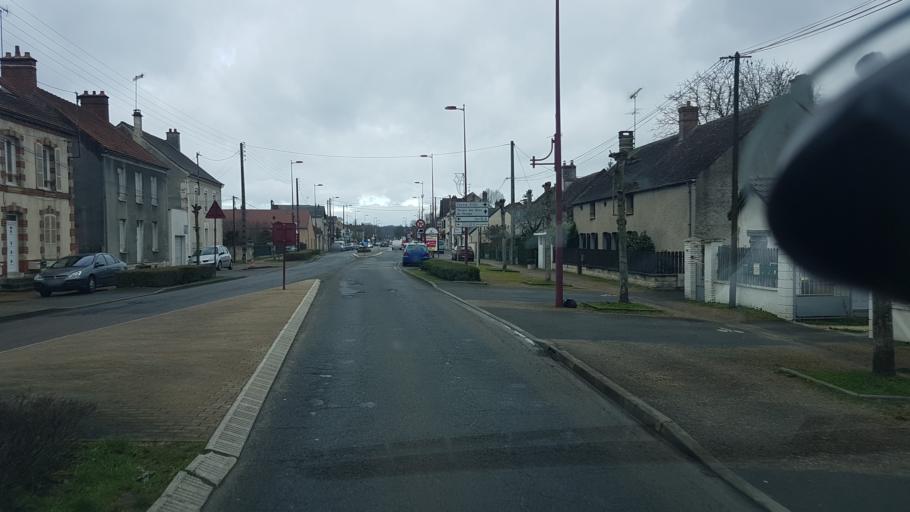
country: FR
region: Centre
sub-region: Departement du Loiret
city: Dordives
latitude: 48.1457
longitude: 2.7640
